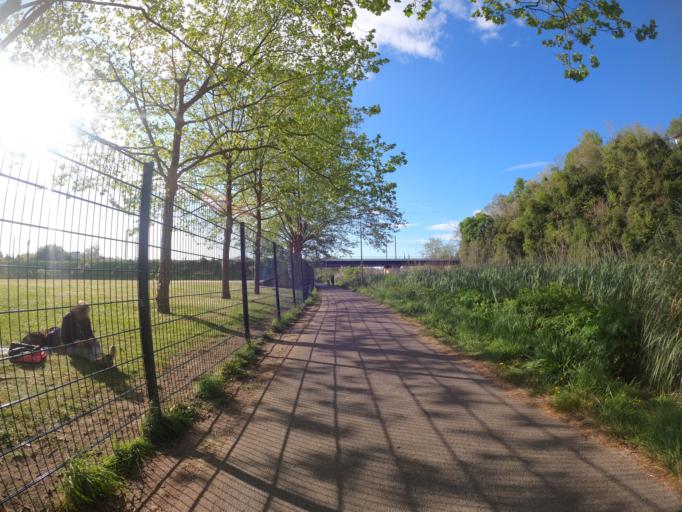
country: FR
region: Aquitaine
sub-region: Departement des Pyrenees-Atlantiques
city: Bayonne
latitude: 43.4818
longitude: -1.4709
